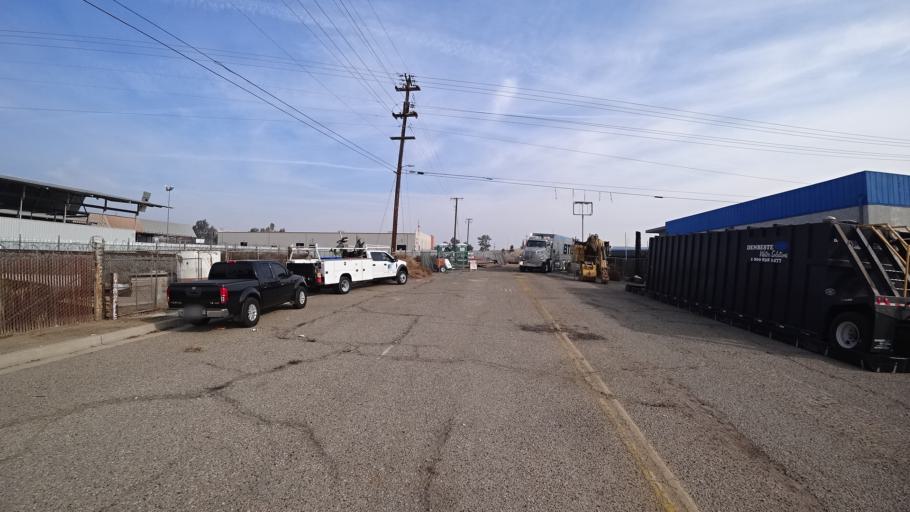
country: US
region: California
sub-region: Kern County
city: Bakersfield
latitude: 35.3810
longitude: -119.0052
